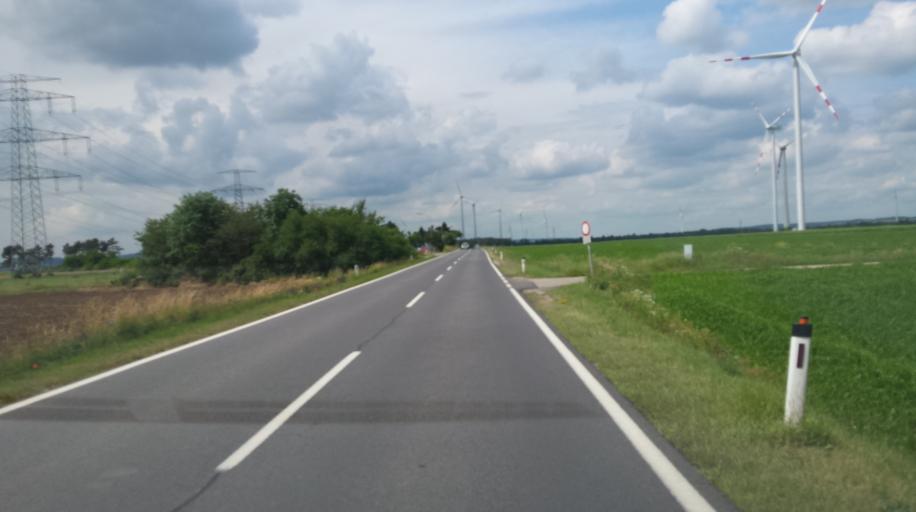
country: AT
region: Lower Austria
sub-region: Politischer Bezirk Ganserndorf
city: Aderklaa
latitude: 48.3156
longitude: 16.5336
